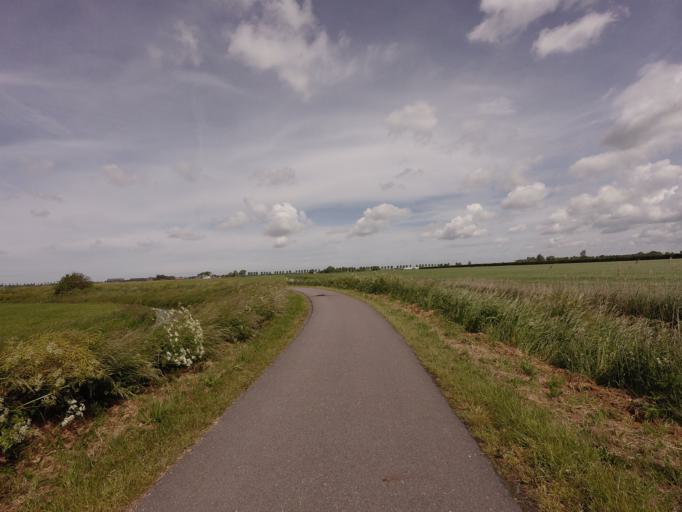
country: NL
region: North Holland
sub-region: Gemeente Opmeer
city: Opmeer
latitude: 52.6739
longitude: 4.9891
